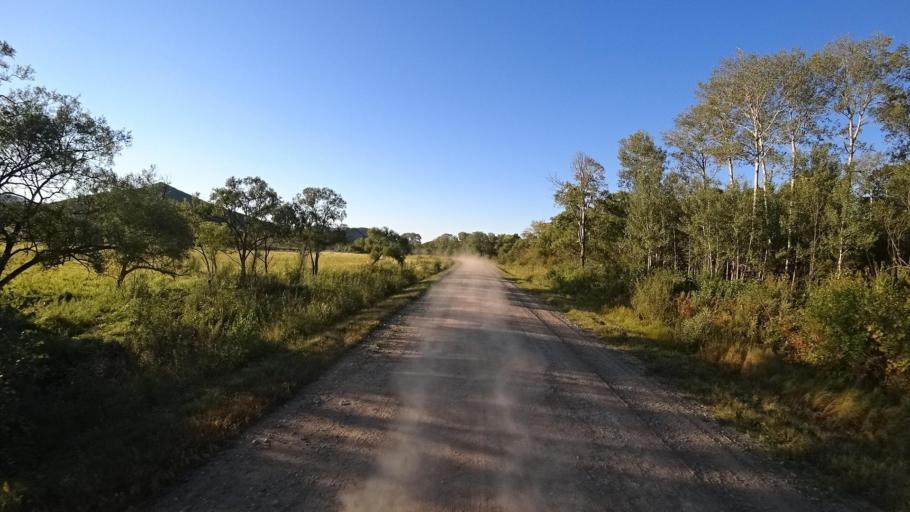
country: RU
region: Primorskiy
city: Kirovskiy
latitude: 44.8315
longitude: 133.5893
